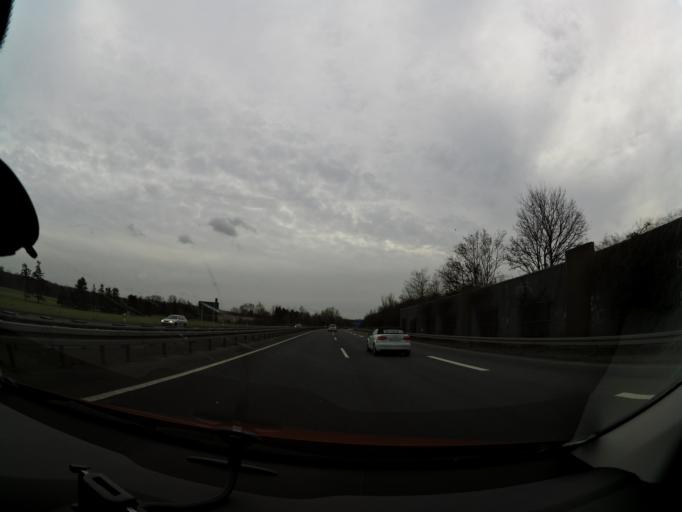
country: DE
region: Lower Saxony
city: Leiferde
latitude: 52.2130
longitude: 10.5342
